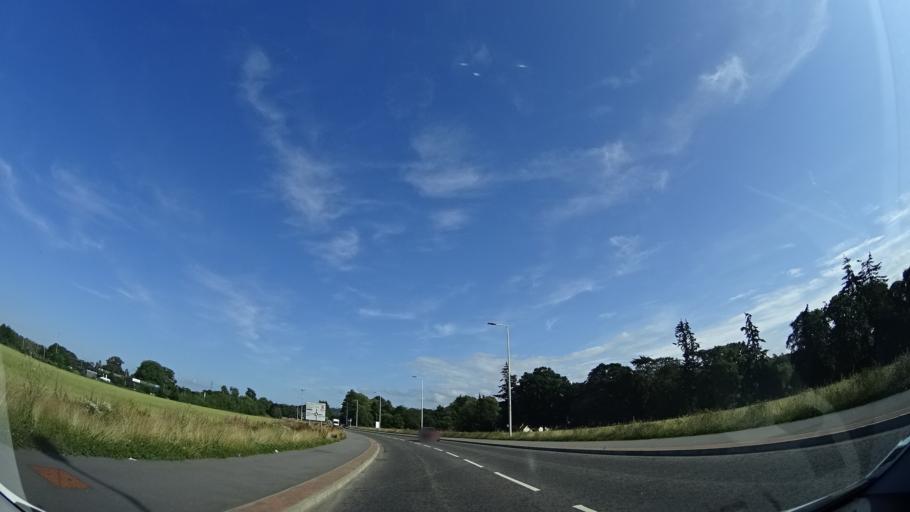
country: GB
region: Scotland
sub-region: Highland
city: Inverness
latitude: 57.4512
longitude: -4.2549
